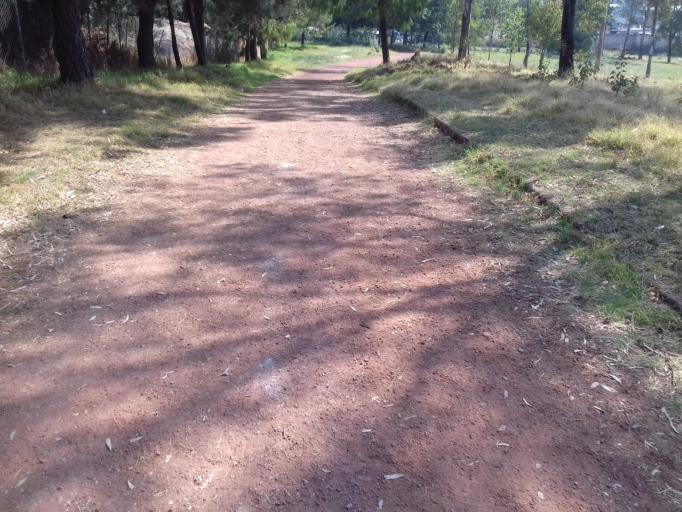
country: MX
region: Mexico
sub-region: Toluca
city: San Antonio Buenavista
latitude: 19.2783
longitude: -99.6964
